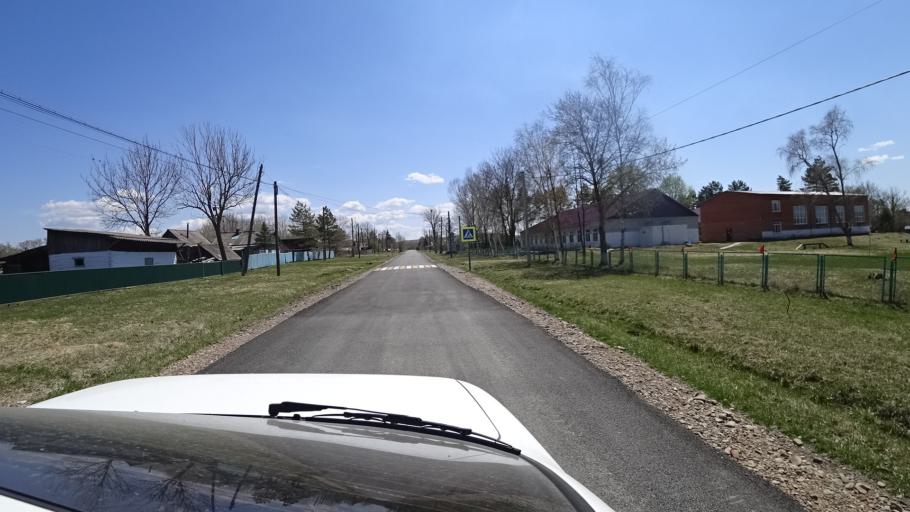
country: RU
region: Primorskiy
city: Dal'nerechensk
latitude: 45.7954
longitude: 133.7682
